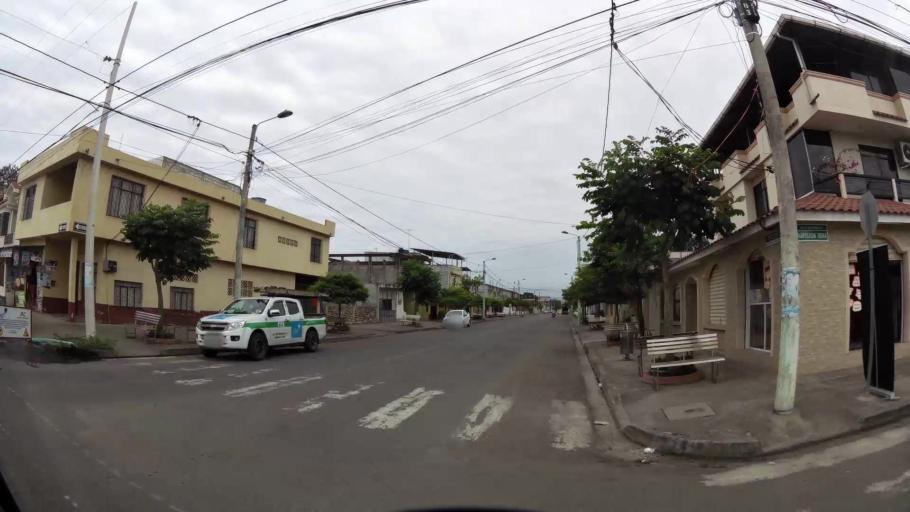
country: EC
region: El Oro
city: Machala
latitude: -3.2562
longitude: -79.9468
